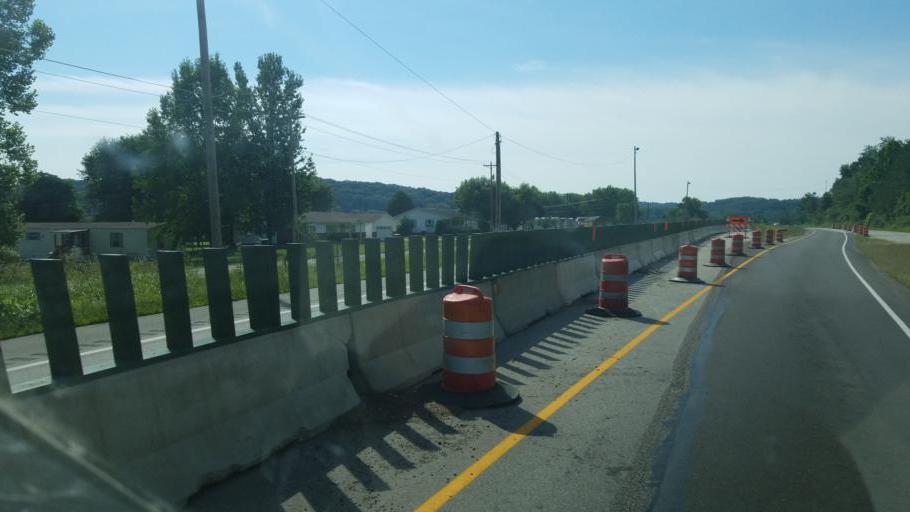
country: US
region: Ohio
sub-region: Athens County
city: Chauncey
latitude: 39.4064
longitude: -82.1800
